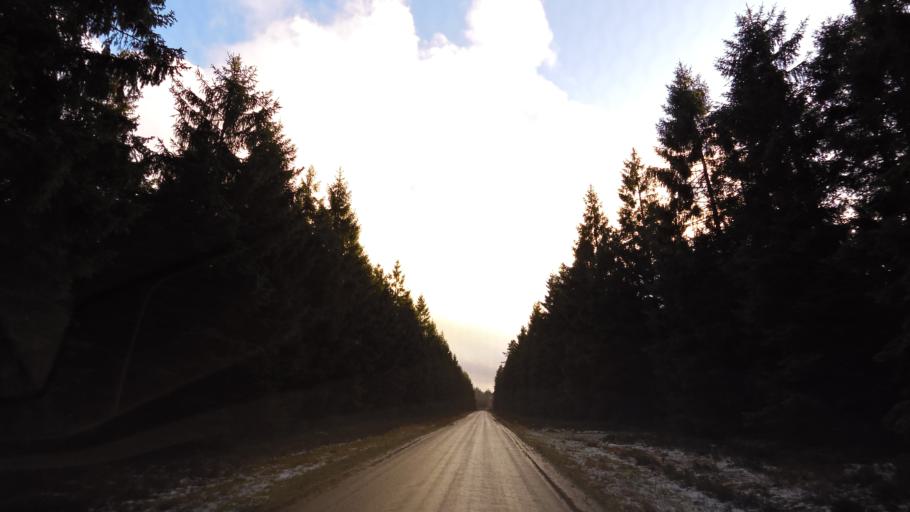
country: DK
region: Central Jutland
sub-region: Ikast-Brande Kommune
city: Brande
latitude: 56.0074
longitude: 9.1663
